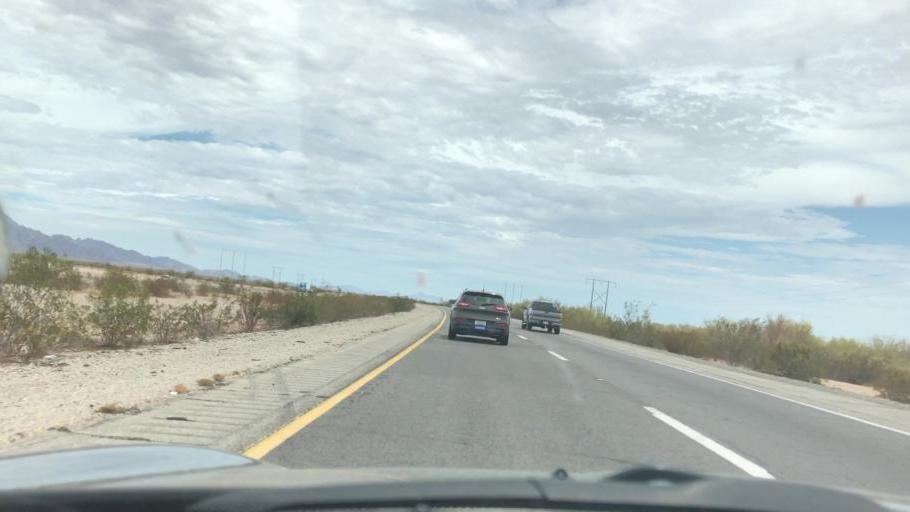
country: US
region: California
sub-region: Riverside County
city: Mesa Verde
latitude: 33.6060
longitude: -114.9832
